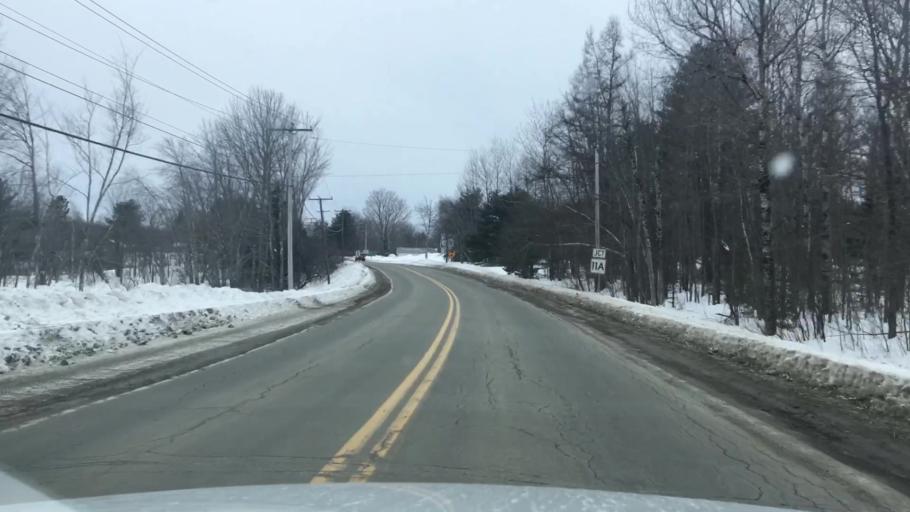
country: US
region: Maine
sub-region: Penobscot County
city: Charleston
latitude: 45.0533
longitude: -69.0270
